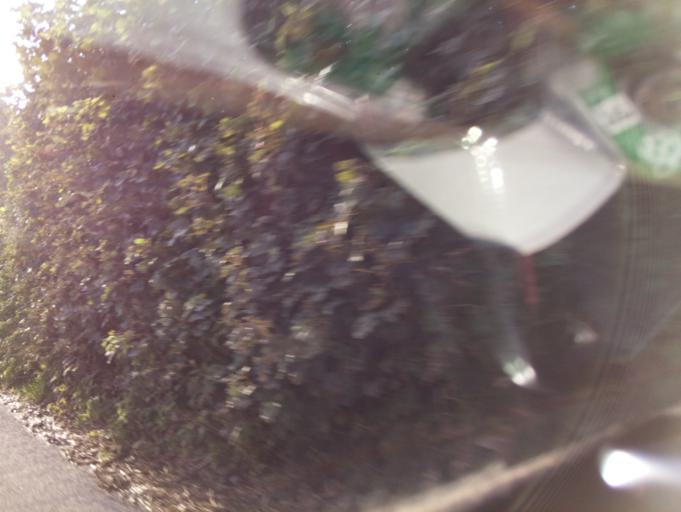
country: GB
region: England
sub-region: Devon
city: Totnes
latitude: 50.3457
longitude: -3.6732
